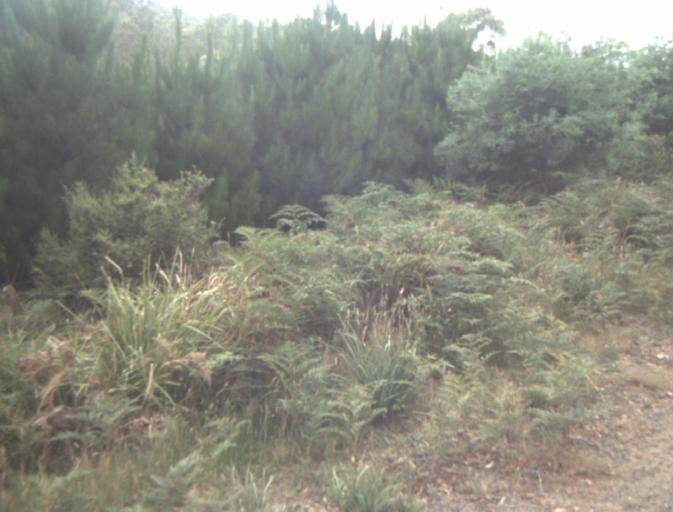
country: AU
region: Tasmania
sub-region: Dorset
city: Scottsdale
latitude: -41.4536
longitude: 147.5285
